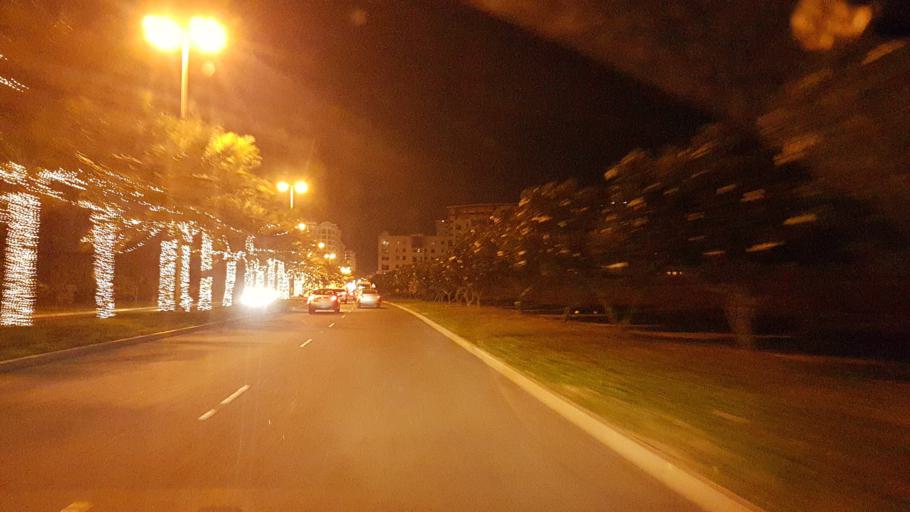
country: BH
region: Muharraq
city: Al Hadd
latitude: 26.2816
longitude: 50.6646
